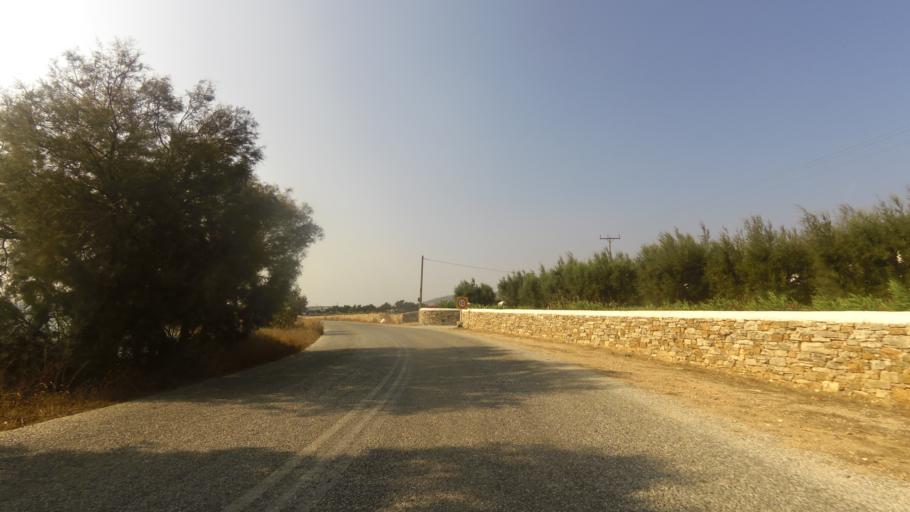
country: GR
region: South Aegean
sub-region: Nomos Kykladon
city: Antiparos
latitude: 37.0143
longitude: 25.0750
